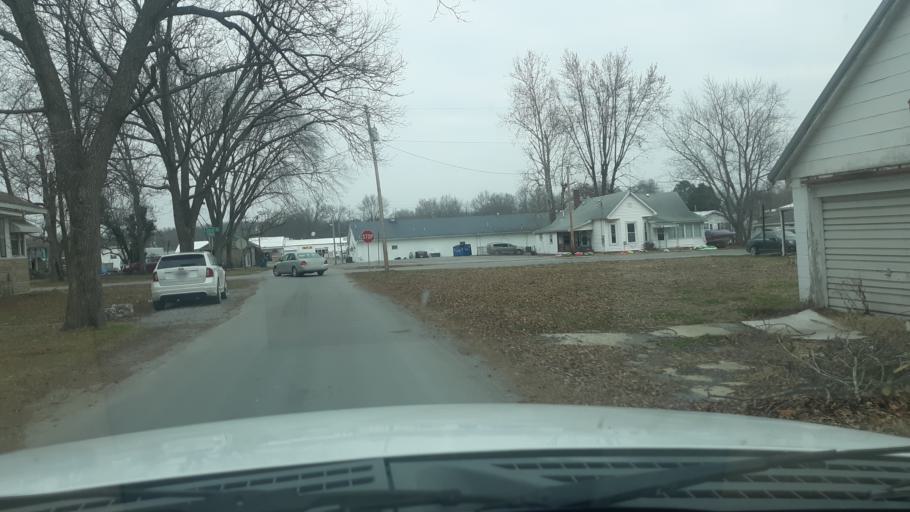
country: US
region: Illinois
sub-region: Saline County
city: Harrisburg
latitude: 37.8394
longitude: -88.6094
